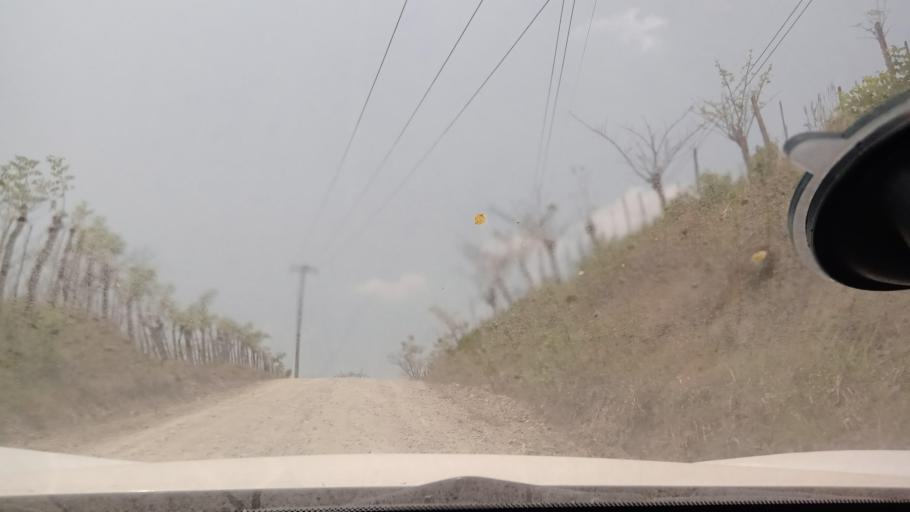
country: MX
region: Chiapas
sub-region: Tecpatan
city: Raudales Malpaso
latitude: 17.4468
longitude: -93.7894
